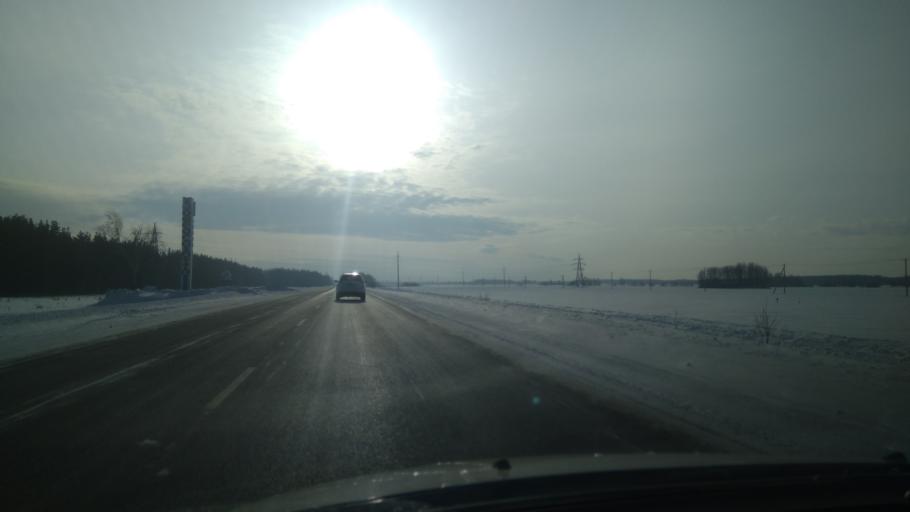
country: RU
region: Sverdlovsk
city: Sukhoy Log
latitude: 56.8672
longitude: 62.0469
